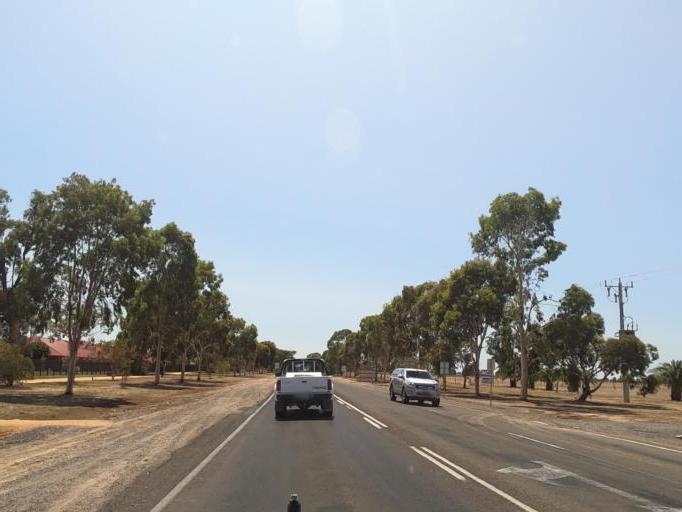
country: AU
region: Victoria
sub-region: Moira
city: Yarrawonga
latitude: -36.0149
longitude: 146.0135
